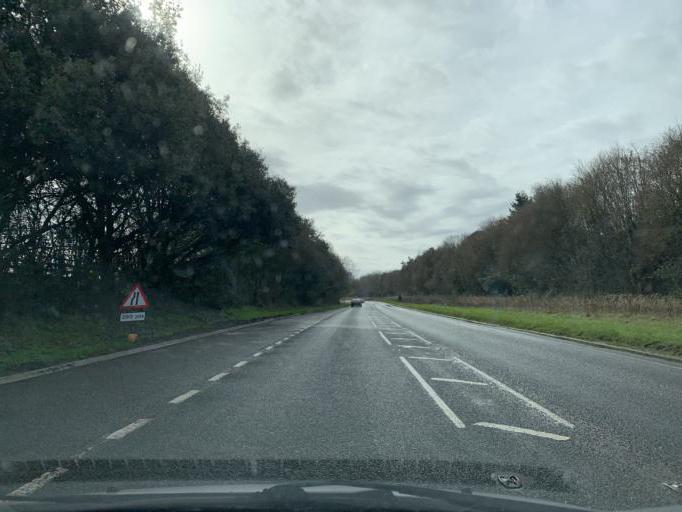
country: GB
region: England
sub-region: Hampshire
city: Fordingbridge
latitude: 50.9335
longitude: -1.7853
